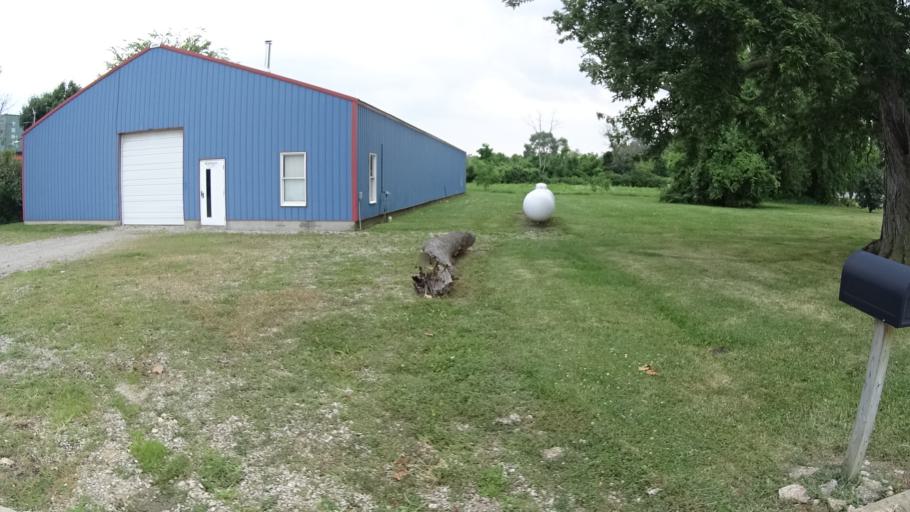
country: US
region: Ohio
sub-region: Erie County
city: Sandusky
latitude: 41.4428
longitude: -82.7467
